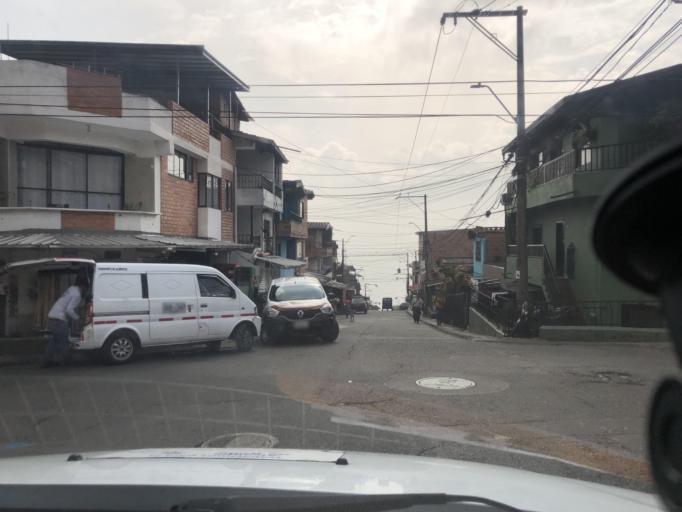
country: CO
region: Antioquia
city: Bello
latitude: 6.3137
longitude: -75.5788
